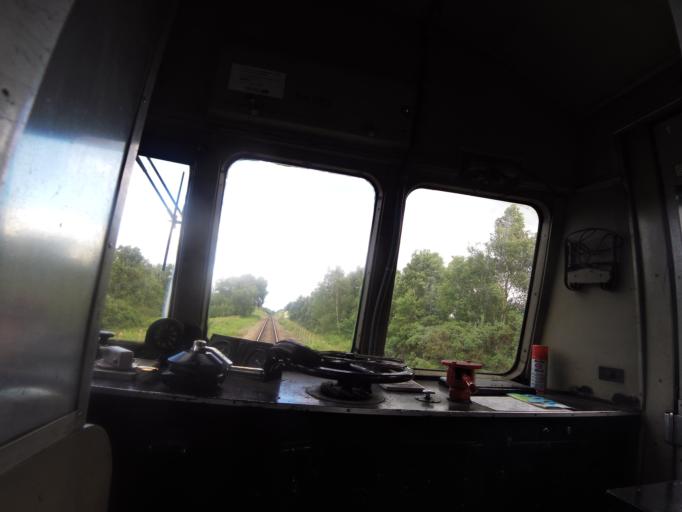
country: GB
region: England
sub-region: Norfolk
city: Sheringham
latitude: 52.9287
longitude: 1.1240
